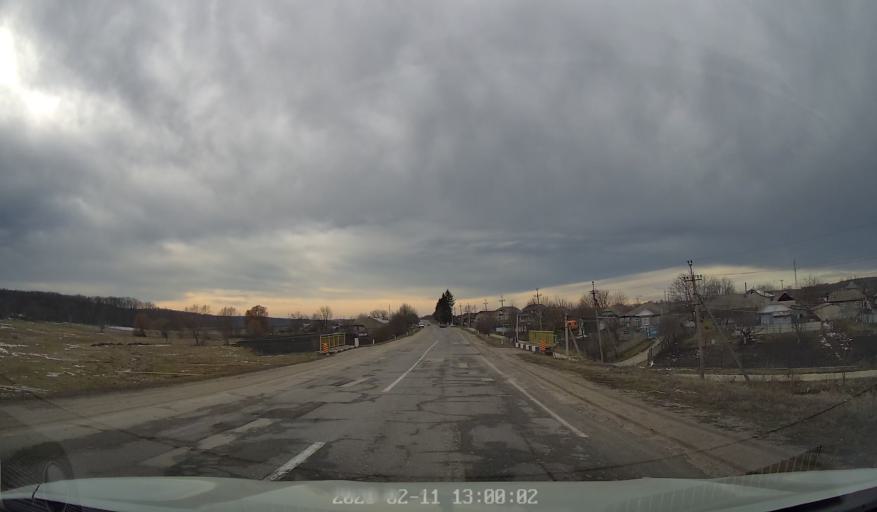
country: MD
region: Briceni
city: Briceni
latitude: 48.3265
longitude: 27.0235
